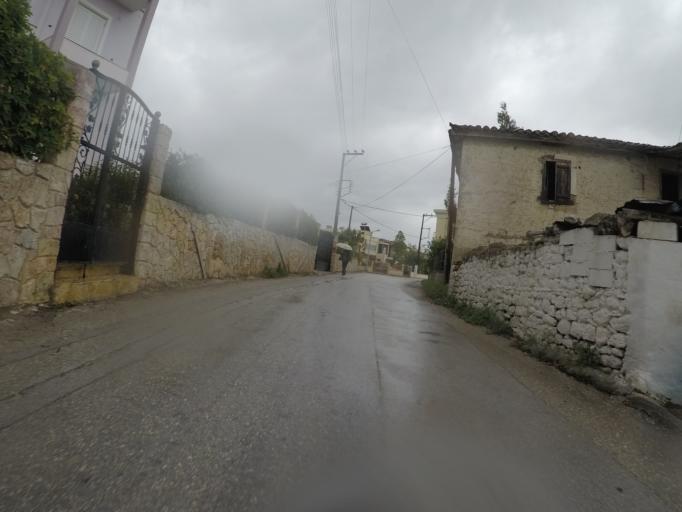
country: GR
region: Peloponnese
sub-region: Nomos Korinthias
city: Arkhaia Korinthos
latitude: 37.9069
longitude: 22.8837
